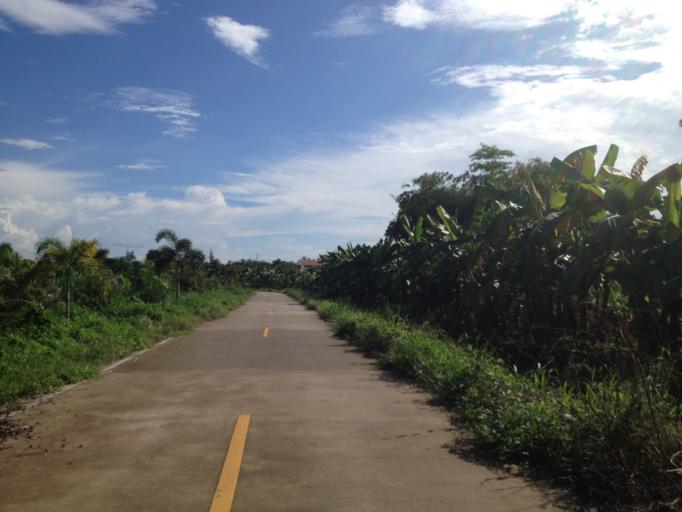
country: TH
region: Chiang Mai
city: Hang Dong
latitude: 18.6924
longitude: 98.8988
